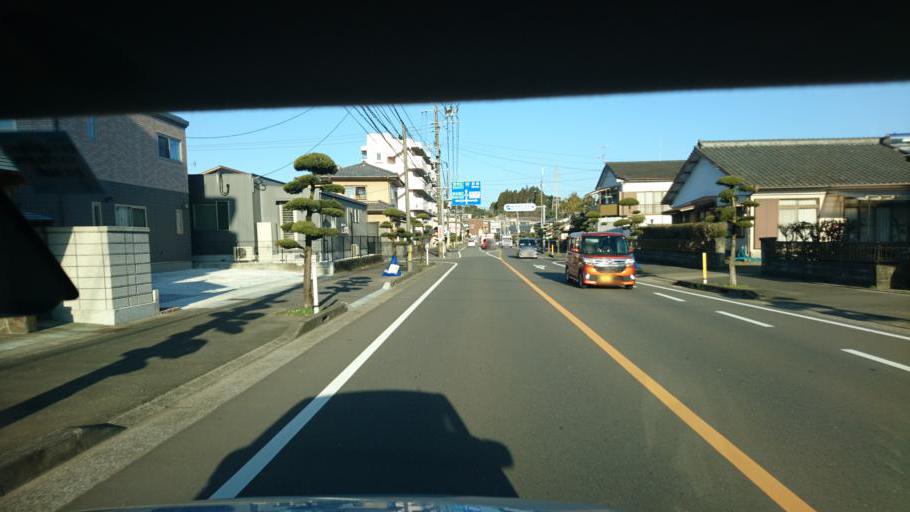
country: JP
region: Miyazaki
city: Miyazaki-shi
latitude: 31.8484
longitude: 131.3892
